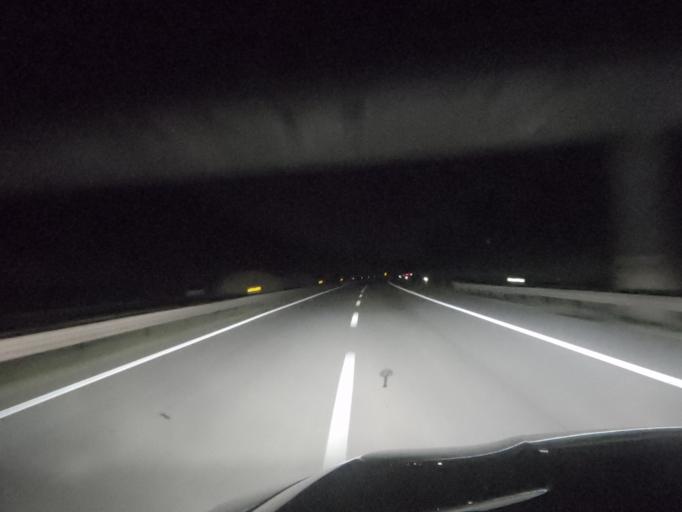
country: PT
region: Aveiro
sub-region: Estarreja
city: Salreu
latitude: 40.7170
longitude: -8.5223
